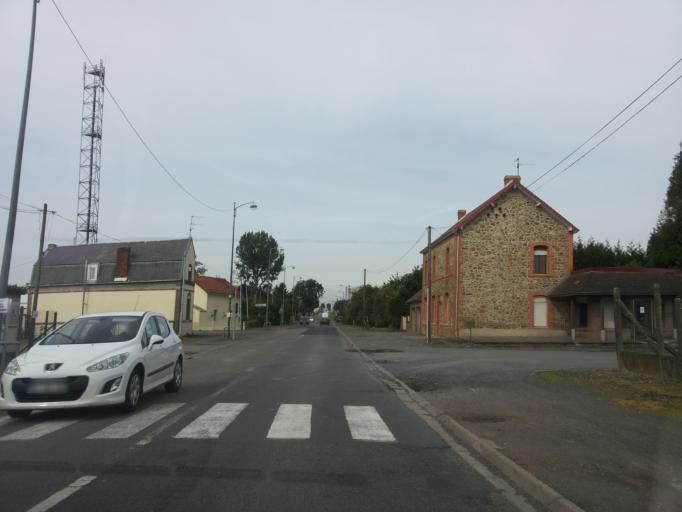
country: FR
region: Nord-Pas-de-Calais
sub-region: Departement du Pas-de-Calais
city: Marquion
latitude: 50.2134
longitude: 3.0774
